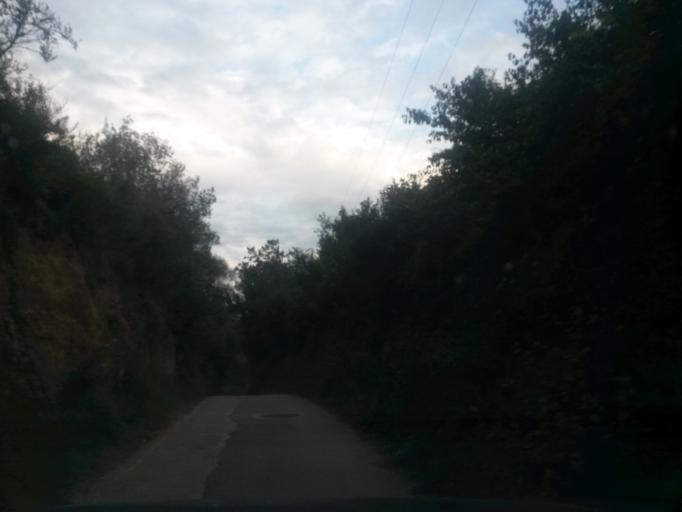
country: ES
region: Catalonia
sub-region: Provincia de Girona
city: Bescano
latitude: 41.9683
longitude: 2.7518
